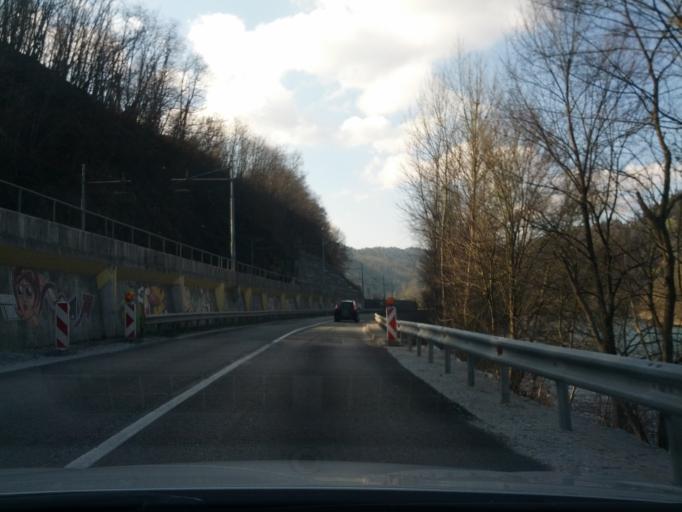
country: SI
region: Litija
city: Litija
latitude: 46.0710
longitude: 14.8212
